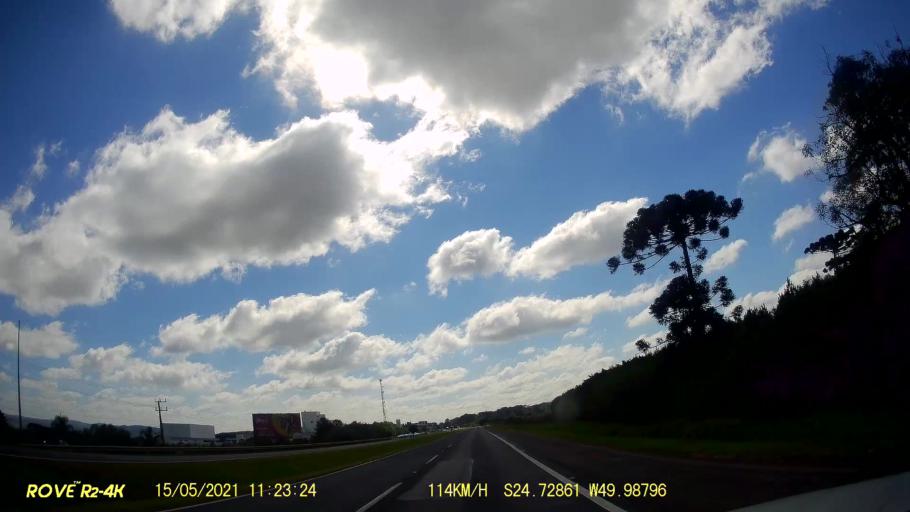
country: BR
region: Parana
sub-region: Castro
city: Castro
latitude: -24.7292
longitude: -49.9879
